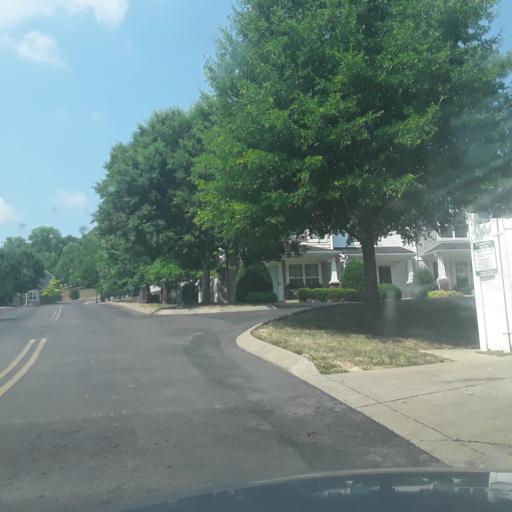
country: US
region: Tennessee
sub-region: Williamson County
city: Brentwood Estates
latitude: 36.0392
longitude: -86.7157
